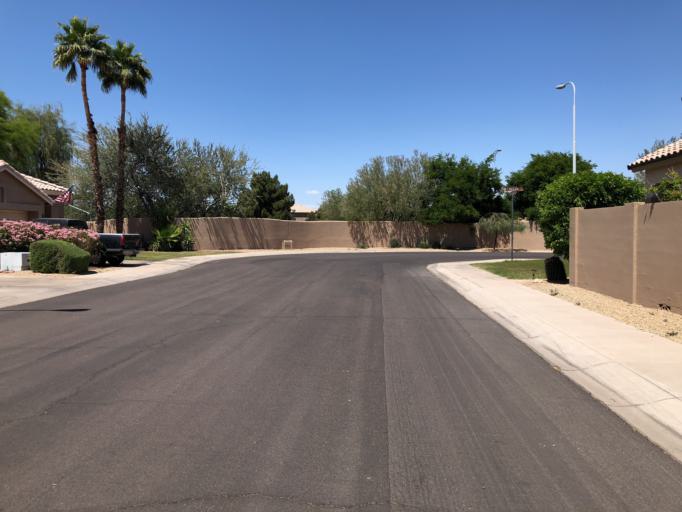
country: US
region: Arizona
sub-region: Maricopa County
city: Guadalupe
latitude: 33.3194
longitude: -111.9320
